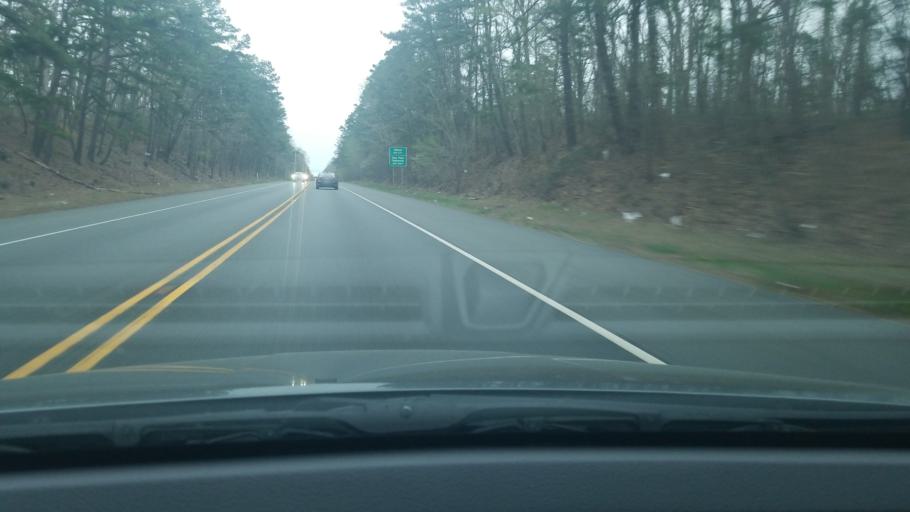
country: US
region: New Jersey
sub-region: Burlington County
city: Leisuretowne
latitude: 39.8857
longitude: -74.6862
